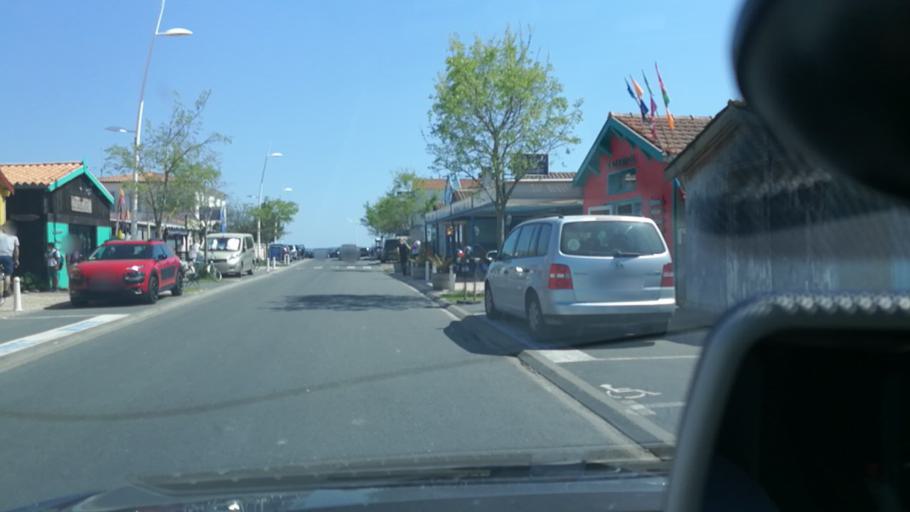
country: FR
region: Poitou-Charentes
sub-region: Departement de la Charente-Maritime
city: Saint-Trojan-les-Bains
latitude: 45.8834
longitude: -1.1920
